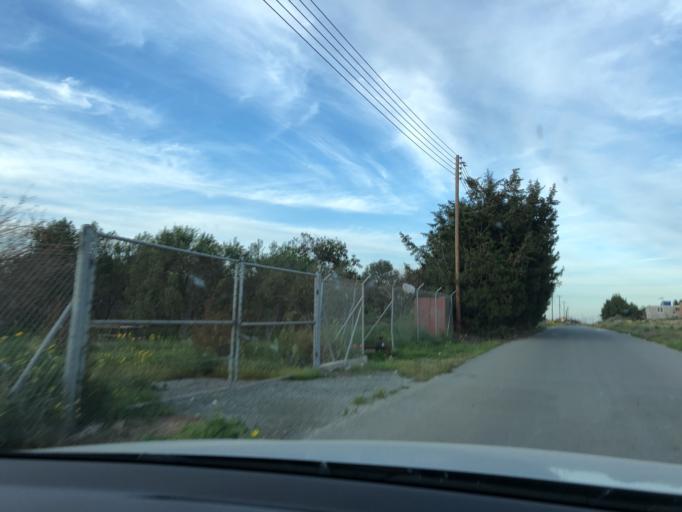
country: CY
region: Larnaka
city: Perivolia
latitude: 34.8336
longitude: 33.5956
